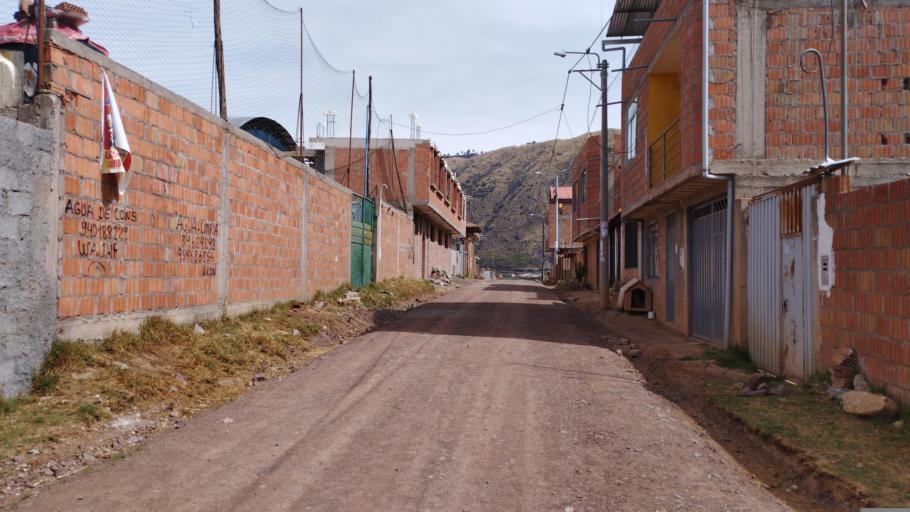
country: PE
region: Cusco
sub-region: Provincia de Cusco
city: Cusco
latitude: -13.5198
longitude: -71.9163
